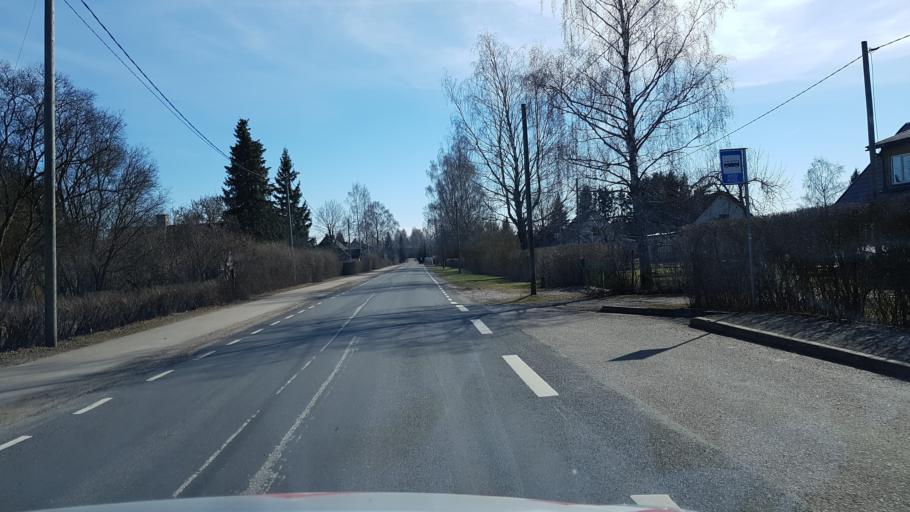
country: EE
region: Harju
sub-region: Nissi vald
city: Riisipere
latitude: 59.1083
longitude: 24.3138
